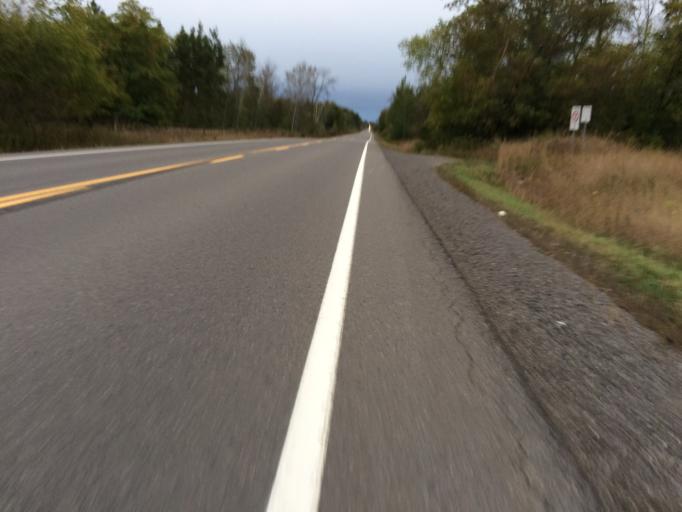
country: CA
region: Ontario
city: Ottawa
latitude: 45.3057
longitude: -75.6431
